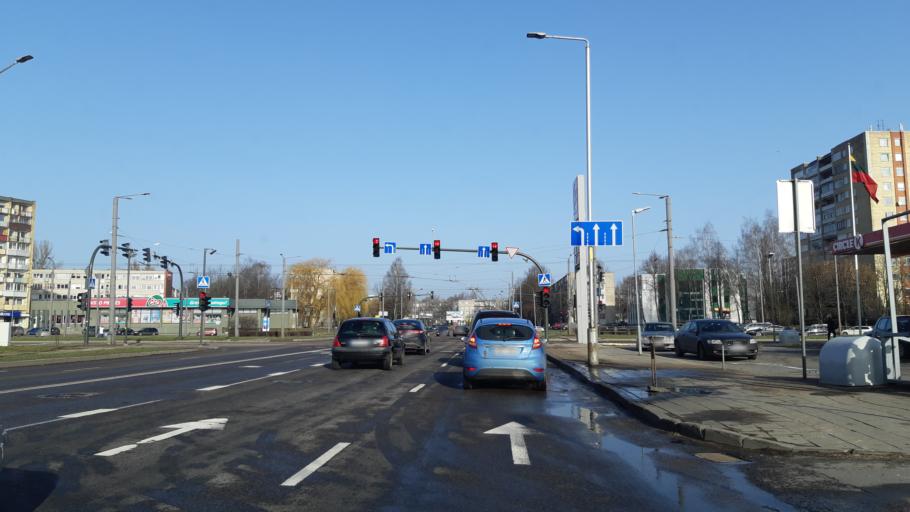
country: LT
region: Kauno apskritis
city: Dainava (Kaunas)
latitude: 54.9117
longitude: 23.9562
